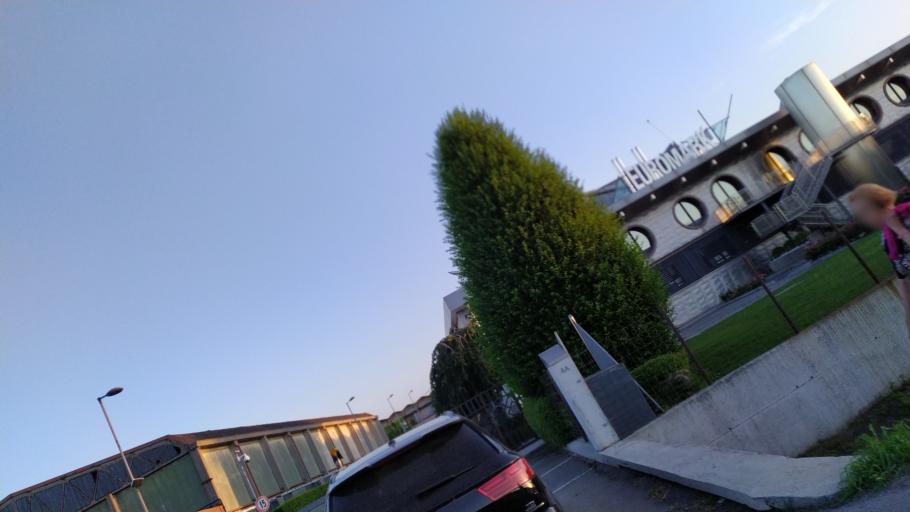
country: IT
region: Veneto
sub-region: Provincia di Padova
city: San Vito
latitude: 45.4243
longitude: 11.9714
